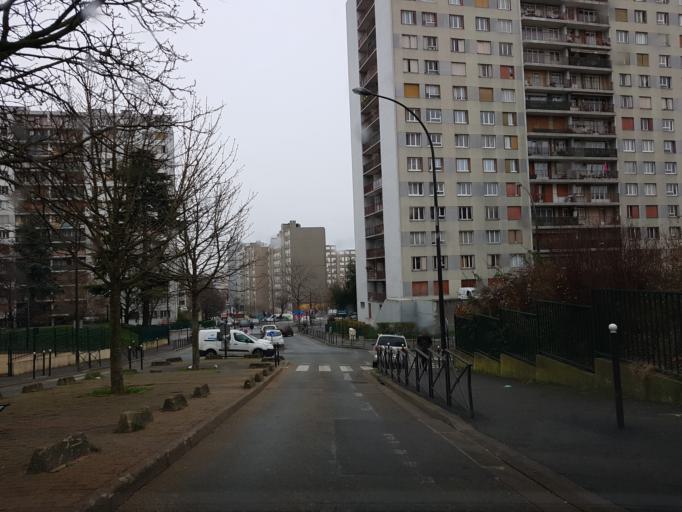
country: FR
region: Ile-de-France
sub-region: Departement du Val-de-Marne
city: Vitry-sur-Seine
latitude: 48.7832
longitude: 2.3893
